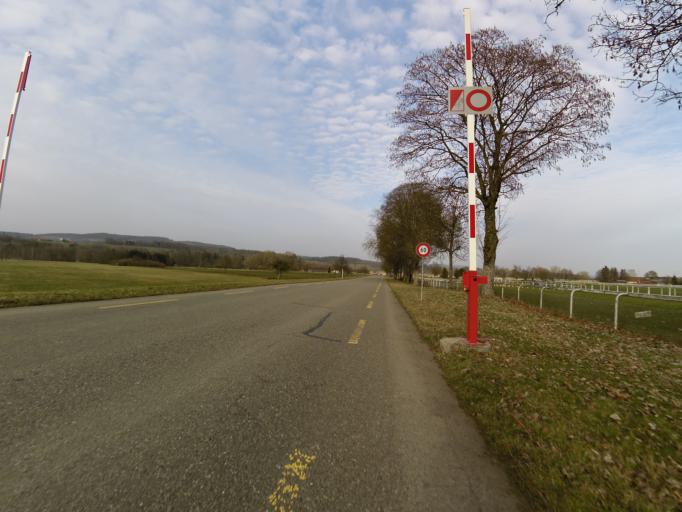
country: CH
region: Thurgau
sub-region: Frauenfeld District
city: Frauenfeld
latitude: 47.5720
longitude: 8.8999
